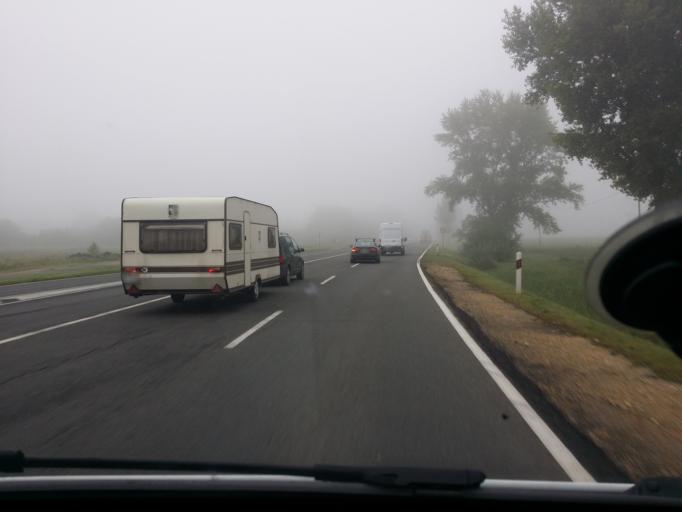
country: HU
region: Bacs-Kiskun
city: Lajosmizse
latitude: 46.9885
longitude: 19.6129
